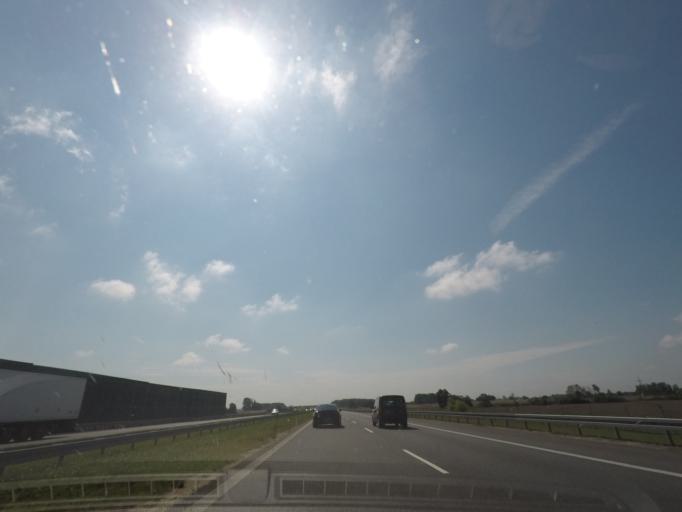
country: PL
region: Lodz Voivodeship
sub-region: Powiat kutnowski
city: Lanieta
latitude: 52.4214
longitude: 19.2595
